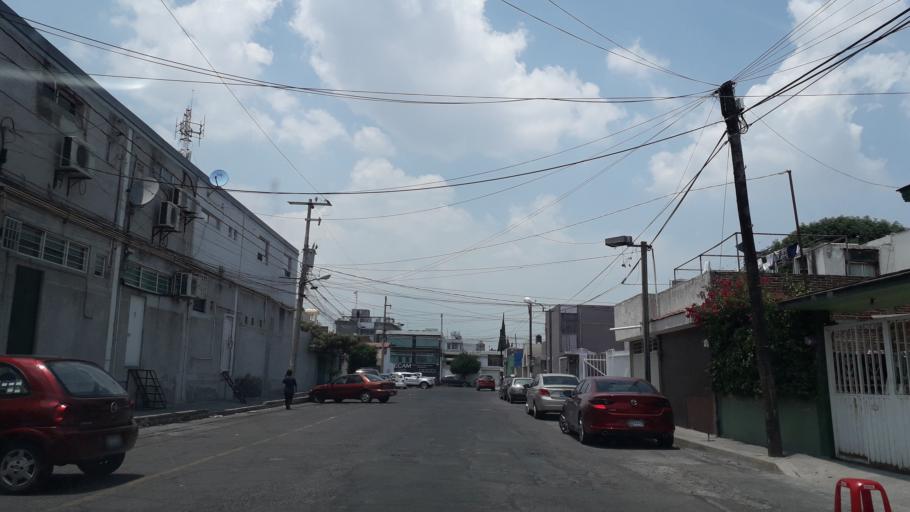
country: MX
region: Puebla
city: Puebla
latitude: 19.0406
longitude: -98.2269
